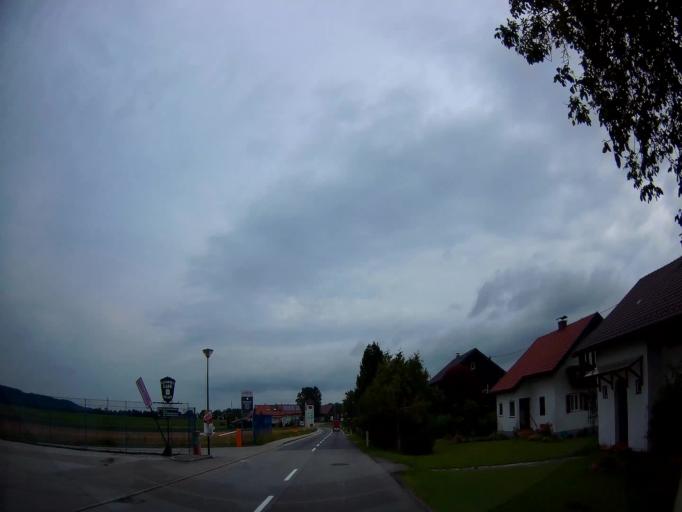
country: AT
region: Salzburg
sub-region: Politischer Bezirk Salzburg-Umgebung
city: Mattsee
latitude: 48.0519
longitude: 13.1493
